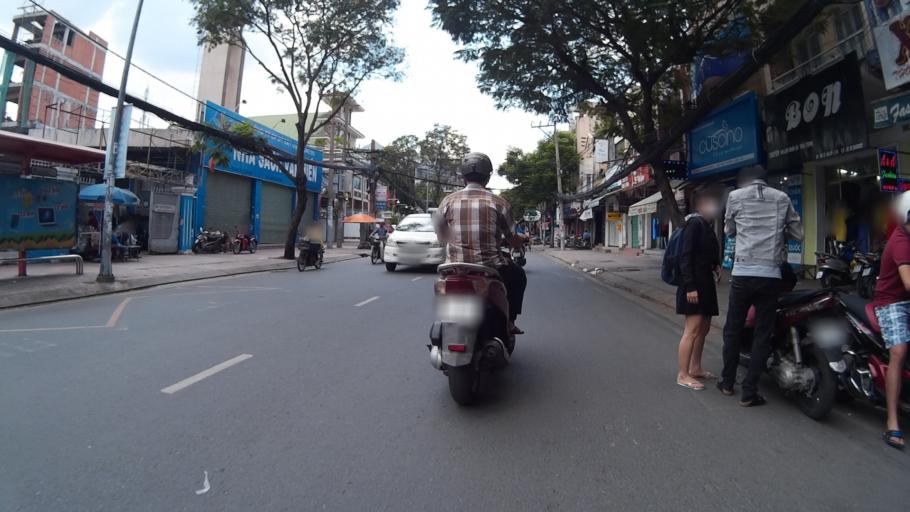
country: VN
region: Ho Chi Minh City
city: Quan Phu Nhuan
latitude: 10.7890
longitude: 106.6758
